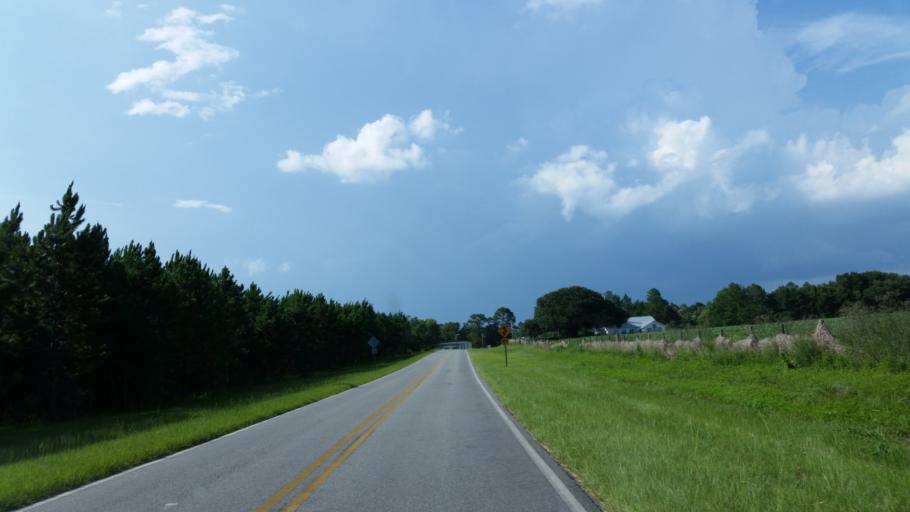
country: US
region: Georgia
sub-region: Lowndes County
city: Hahira
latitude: 30.9363
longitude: -83.4086
